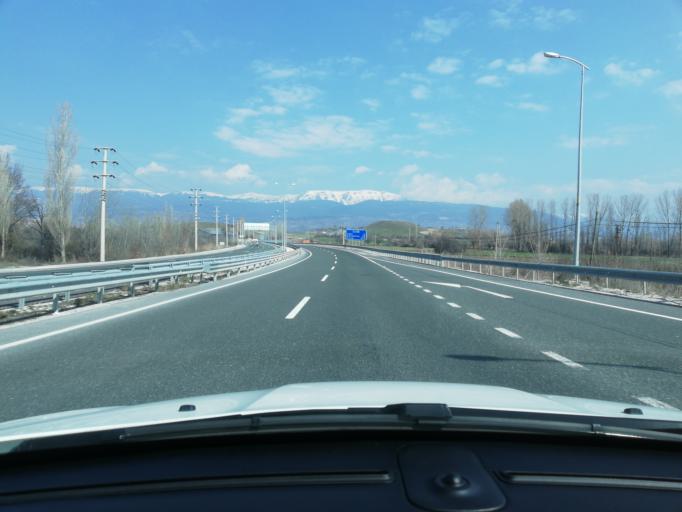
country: TR
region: Cankiri
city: Ilgaz
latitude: 40.9063
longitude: 33.6504
